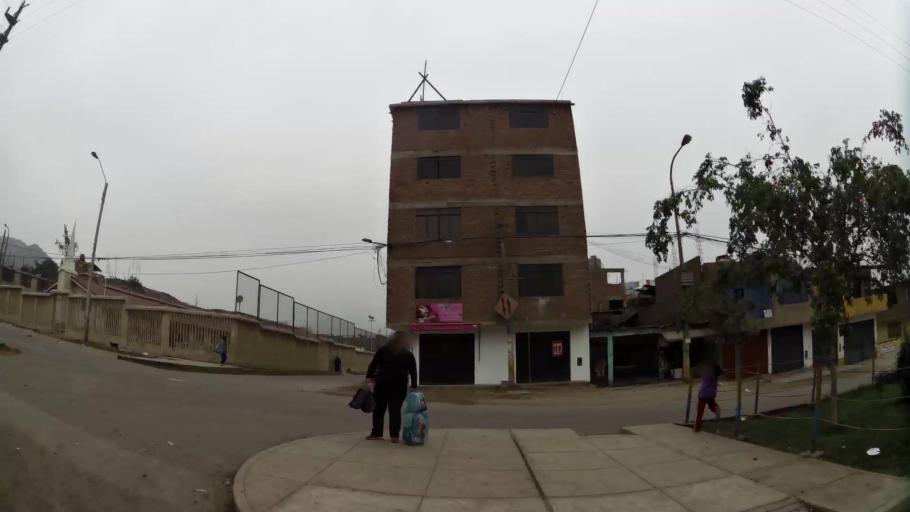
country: PE
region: Lima
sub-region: Lima
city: Independencia
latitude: -11.9403
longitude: -76.9909
